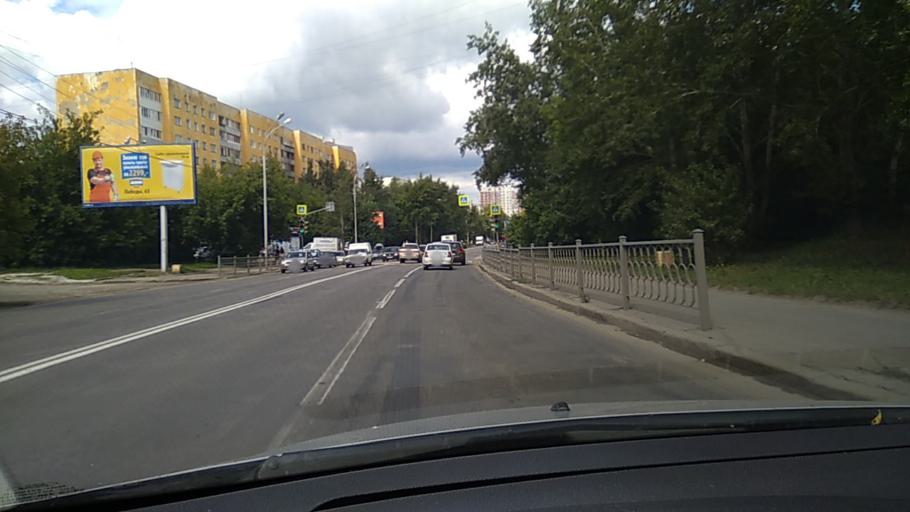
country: RU
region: Sverdlovsk
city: Yekaterinburg
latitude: 56.9038
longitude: 60.6233
